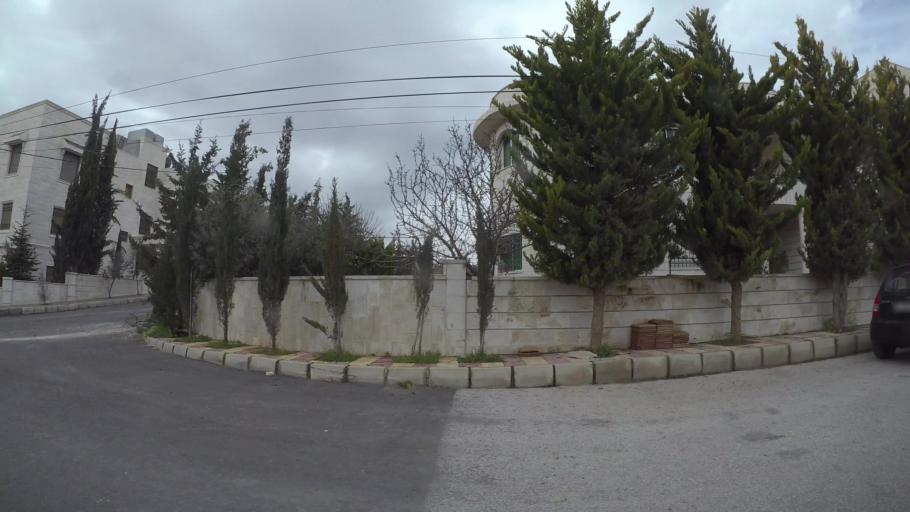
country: JO
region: Amman
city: Umm as Summaq
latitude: 31.9119
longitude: 35.8418
